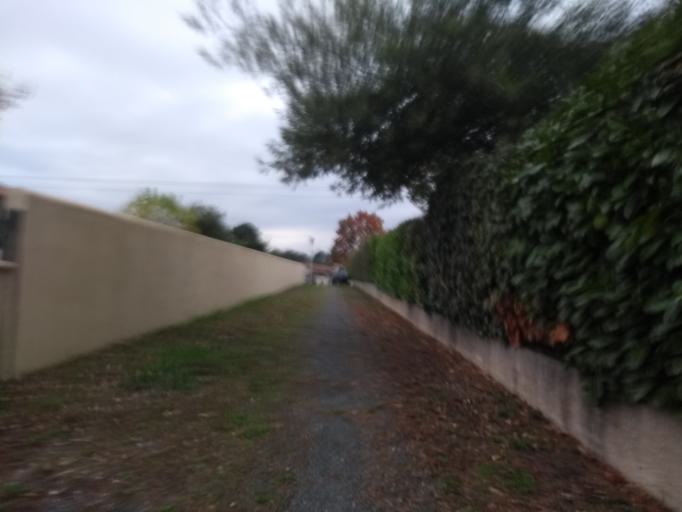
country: FR
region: Aquitaine
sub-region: Departement de la Gironde
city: Talence
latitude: 44.7826
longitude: -0.5909
